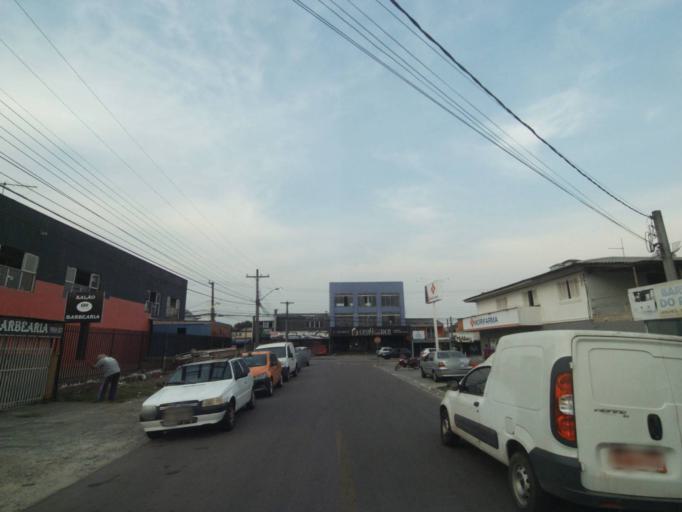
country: BR
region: Parana
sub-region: Sao Jose Dos Pinhais
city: Sao Jose dos Pinhais
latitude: -25.5257
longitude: -49.2688
